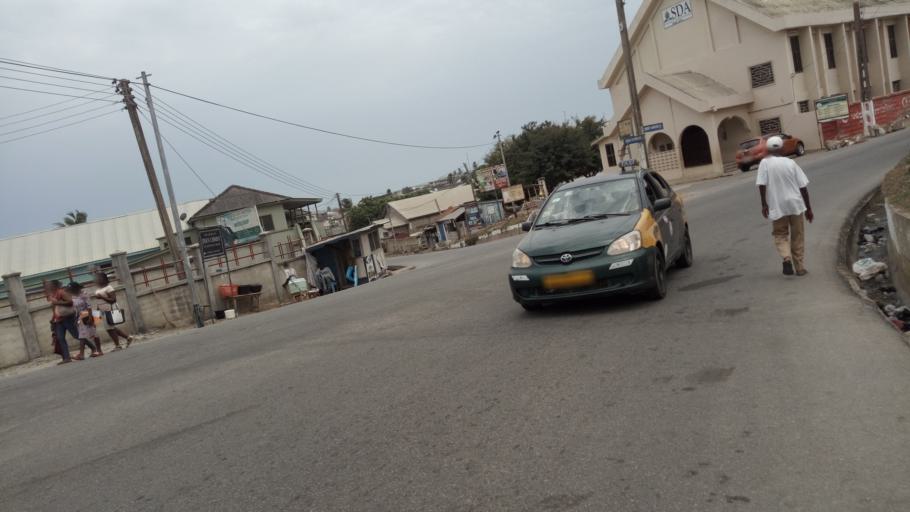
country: GH
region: Central
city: Winneba
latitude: 5.3426
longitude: -0.6240
